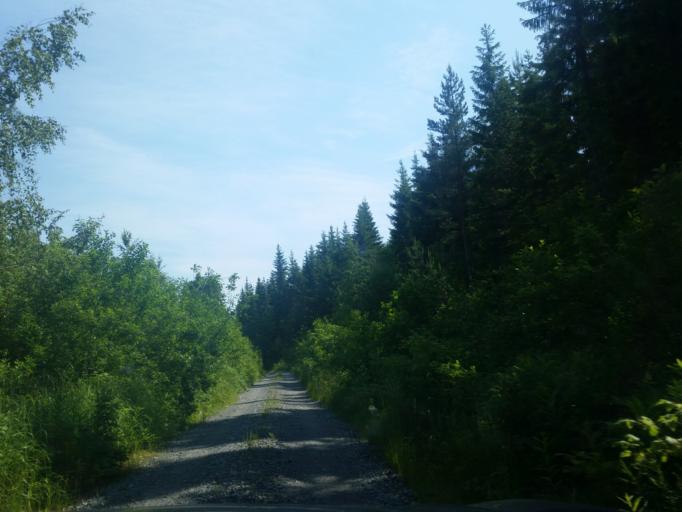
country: FI
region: Northern Savo
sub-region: Ylae-Savo
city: Keitele
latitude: 63.1037
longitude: 26.5410
